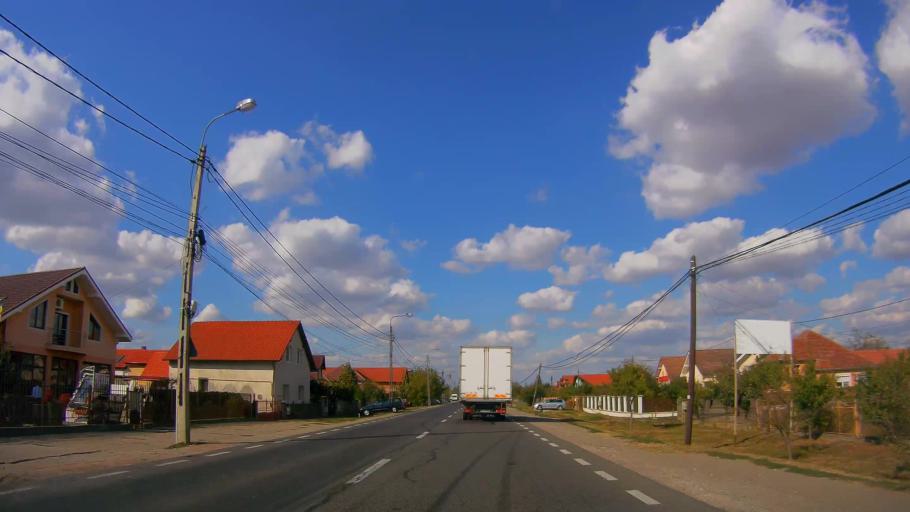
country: RO
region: Satu Mare
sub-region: Oras Ardud
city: Madaras
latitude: 47.7338
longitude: 22.8825
